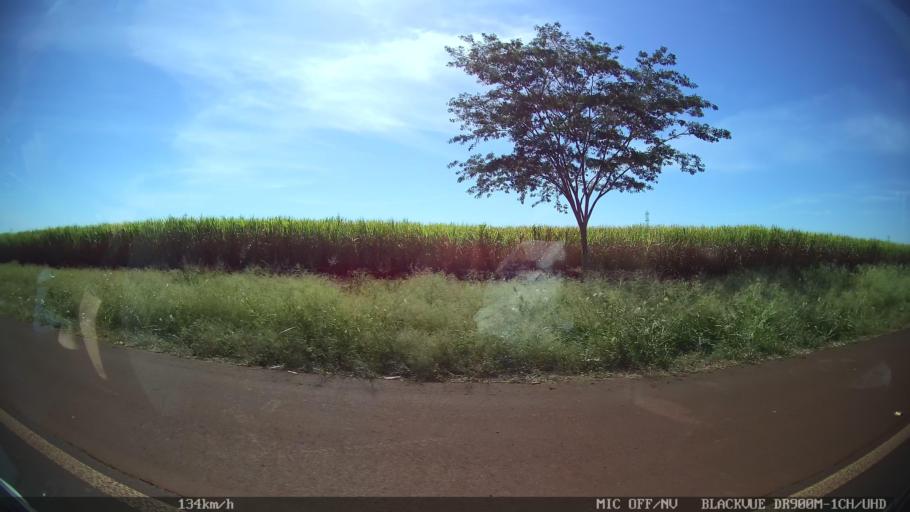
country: BR
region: Sao Paulo
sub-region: Guaira
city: Guaira
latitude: -20.4446
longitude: -48.2614
